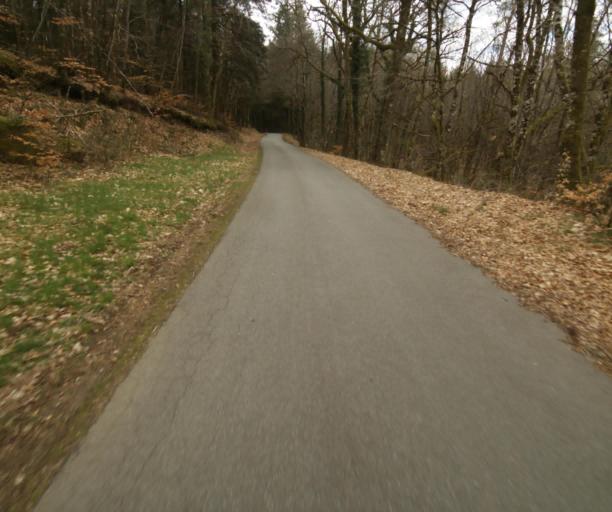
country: FR
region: Limousin
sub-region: Departement de la Correze
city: Correze
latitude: 45.3226
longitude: 1.9431
